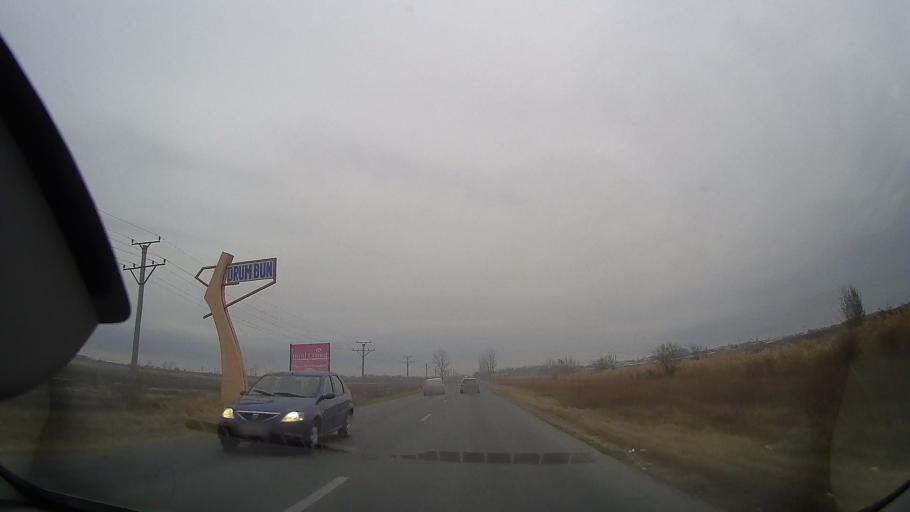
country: RO
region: Ialomita
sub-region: Comuna Slobozia
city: Slobozia
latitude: 44.5816
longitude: 27.3364
